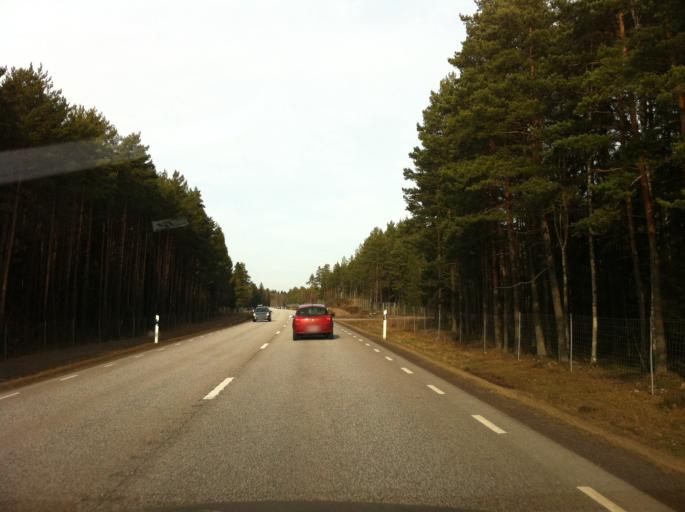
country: SE
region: Vaestra Goetaland
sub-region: Gullspangs Kommun
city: Gullspang
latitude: 58.9118
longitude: 14.0249
